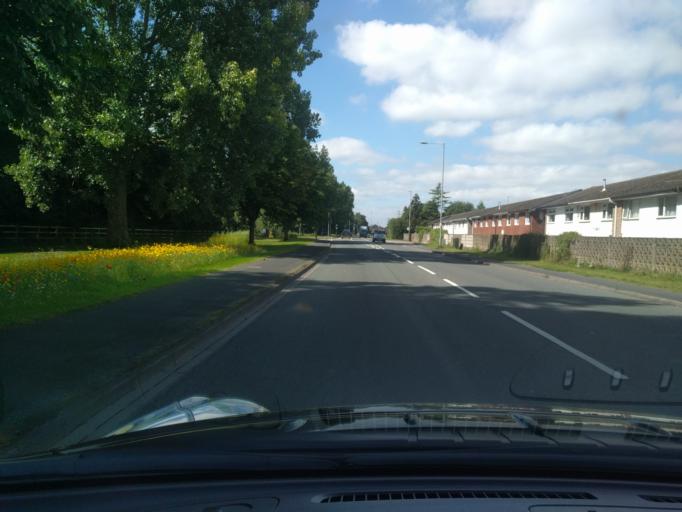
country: GB
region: England
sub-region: Warrington
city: Grappenhall
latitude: 53.3988
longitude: -2.5254
